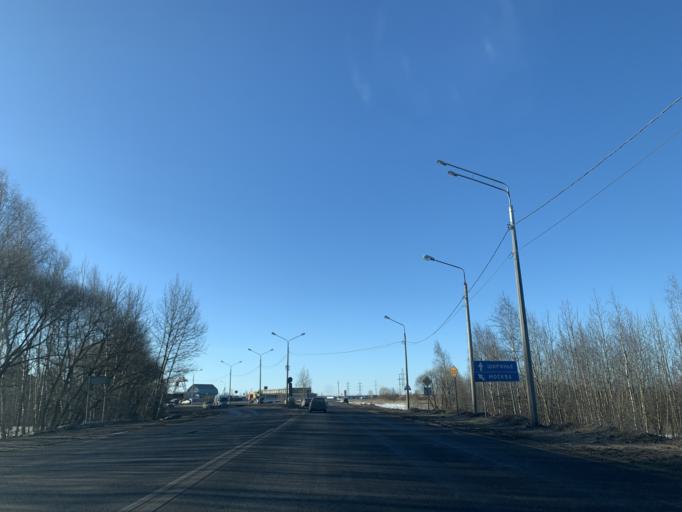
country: RU
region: Jaroslavl
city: Yaroslavl
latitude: 57.6360
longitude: 39.7462
